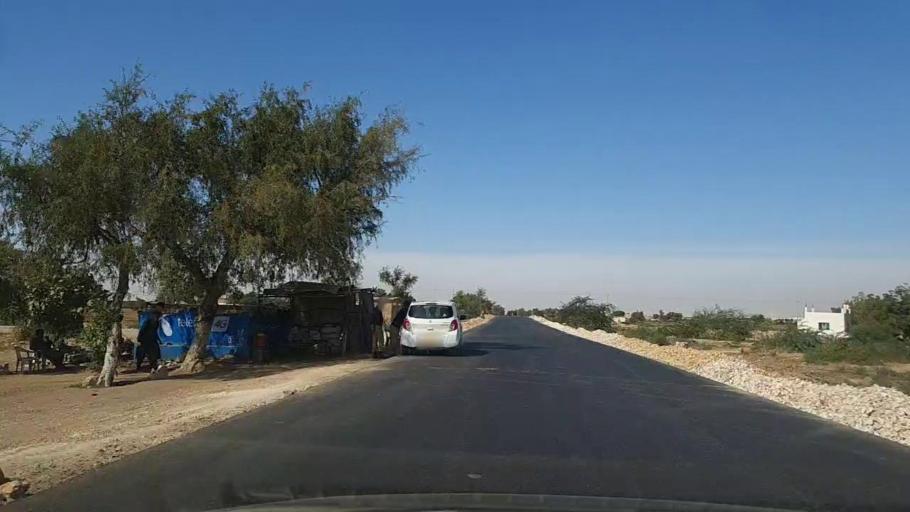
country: PK
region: Sindh
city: Kotri
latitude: 25.2843
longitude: 68.2100
